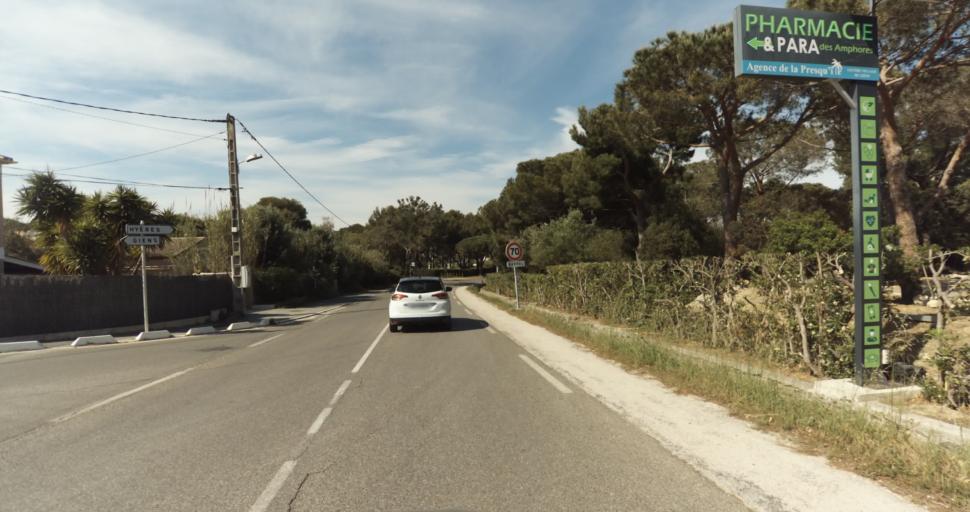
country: FR
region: Provence-Alpes-Cote d'Azur
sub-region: Departement du Var
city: Hyeres
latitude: 43.0362
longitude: 6.1439
